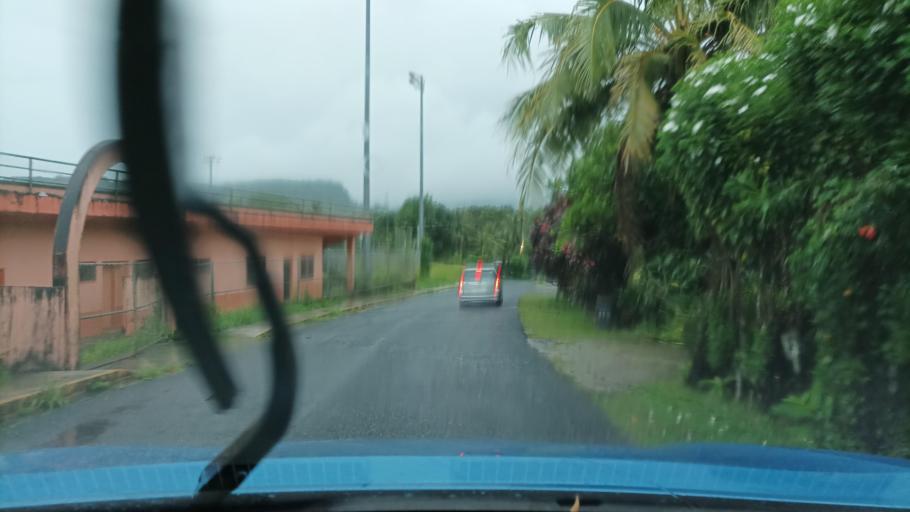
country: FM
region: Pohnpei
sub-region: Kolonia Municipality
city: Kolonia
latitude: 6.9592
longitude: 158.2111
